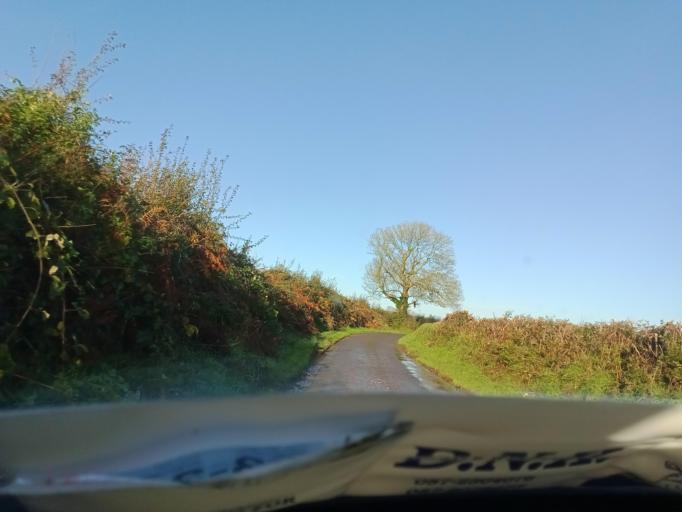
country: IE
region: Munster
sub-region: Waterford
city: Waterford
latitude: 52.2869
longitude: -7.1680
